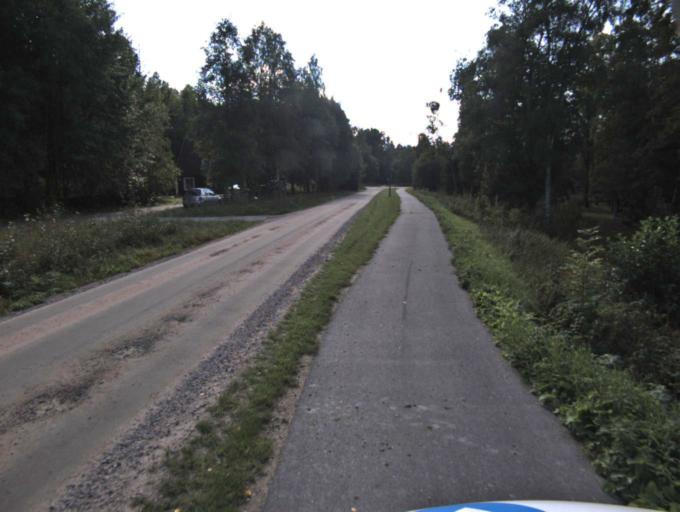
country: SE
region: Vaestra Goetaland
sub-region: Boras Kommun
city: Dalsjofors
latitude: 57.8269
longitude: 13.1959
